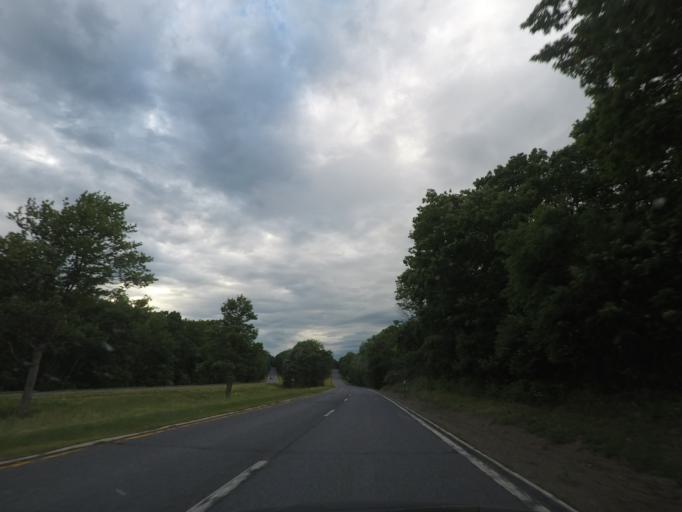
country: US
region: New York
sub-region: Dutchess County
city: Pine Plains
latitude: 41.9650
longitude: -73.7508
